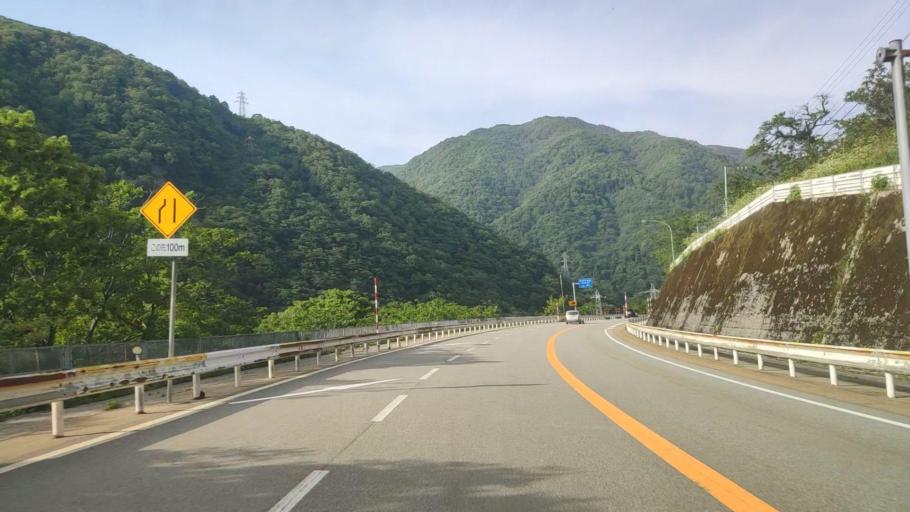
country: JP
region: Toyama
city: Yatsuomachi-higashikumisaka
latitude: 36.3998
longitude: 137.2893
